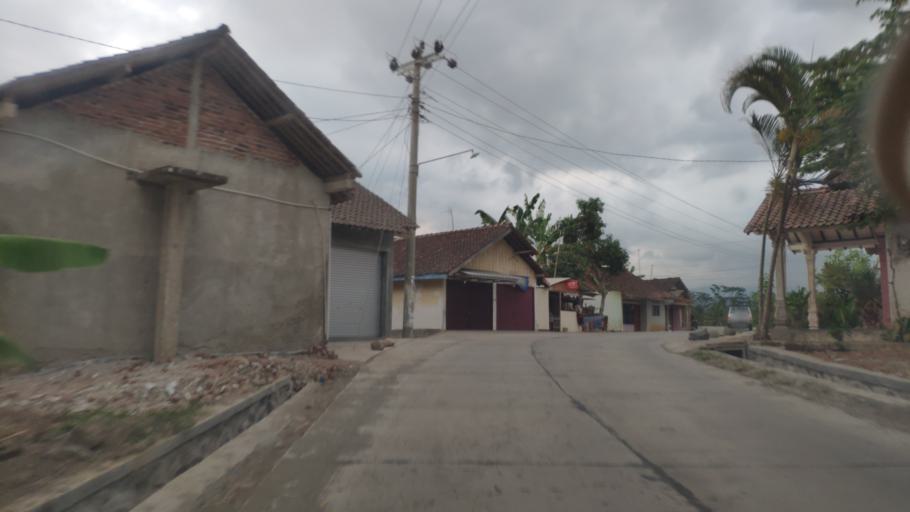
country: ID
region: Central Java
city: Wonosobo
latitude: -7.3763
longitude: 109.6655
